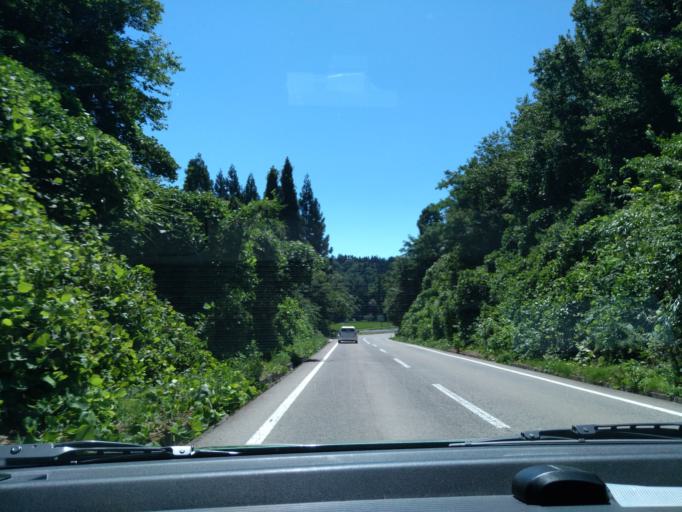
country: JP
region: Akita
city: Yokotemachi
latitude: 39.4191
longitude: 140.5899
